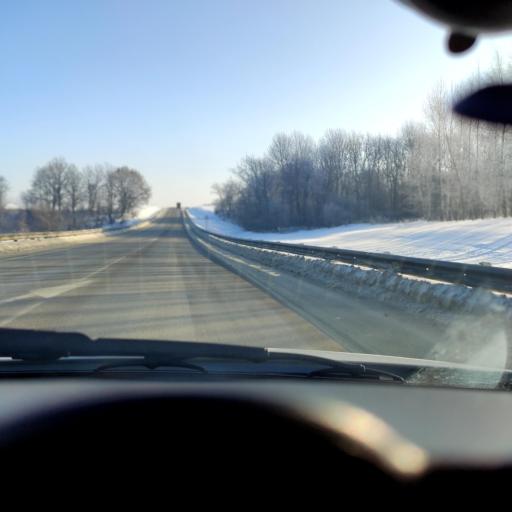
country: RU
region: Kursk
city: Tim
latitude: 51.6525
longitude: 36.9533
